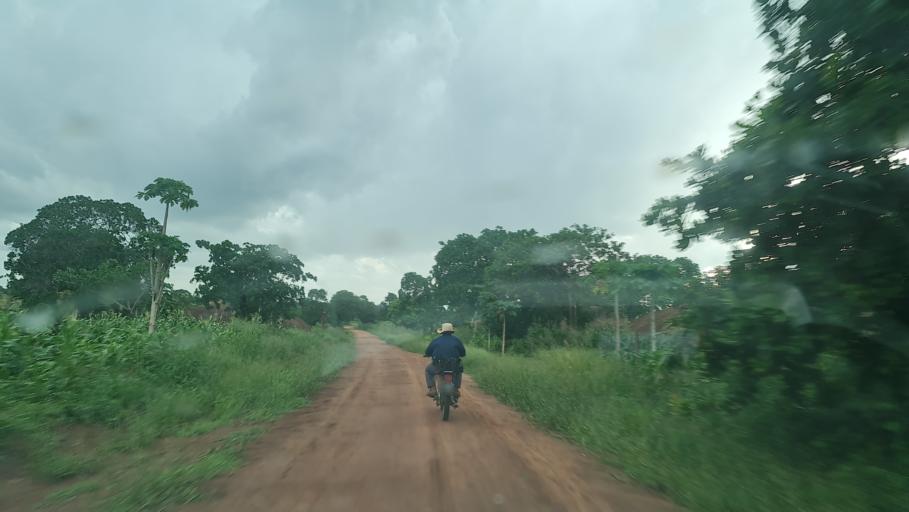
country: MZ
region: Nampula
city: Nacala
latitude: -13.9956
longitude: 40.3642
